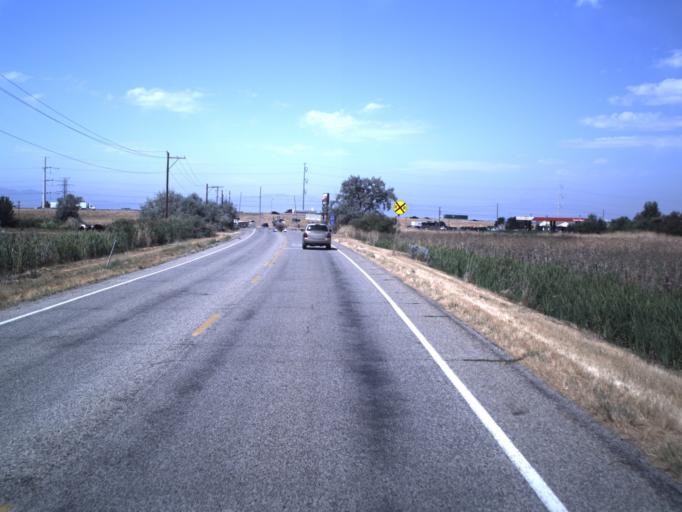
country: US
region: Utah
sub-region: Box Elder County
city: Willard
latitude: 41.4227
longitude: -112.0472
